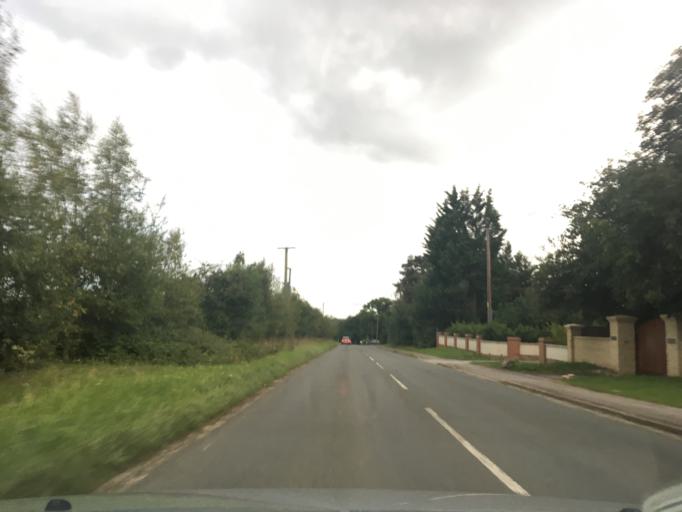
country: GB
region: England
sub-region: Oxfordshire
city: Cowley
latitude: 51.7759
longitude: -1.1887
